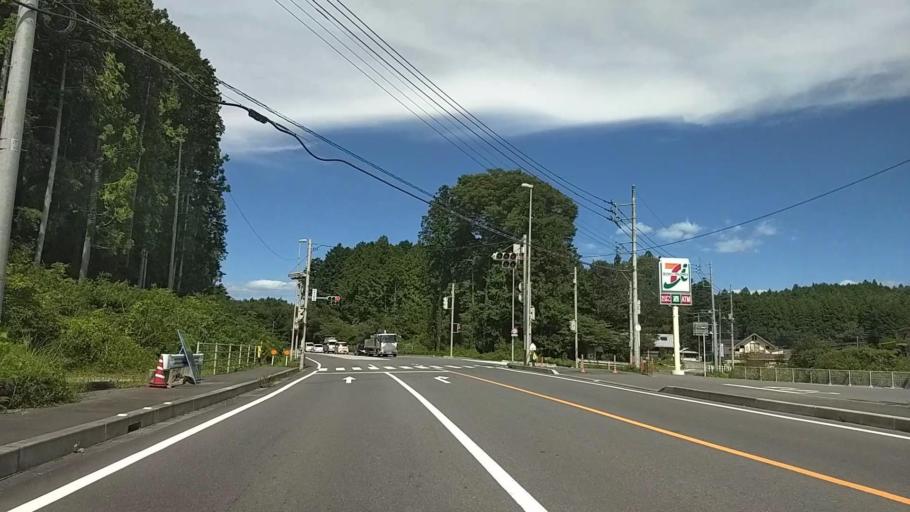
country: JP
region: Tochigi
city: Imaichi
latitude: 36.7008
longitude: 139.7532
